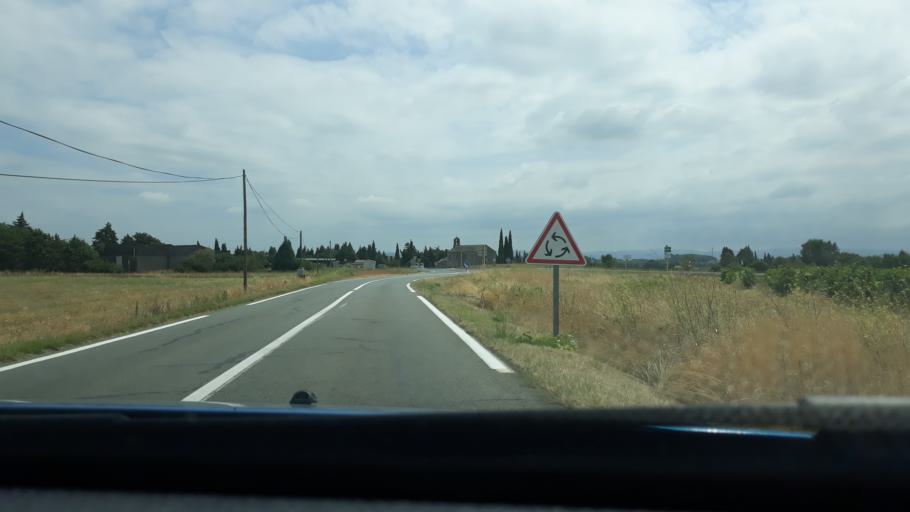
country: FR
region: Languedoc-Roussillon
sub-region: Departement de l'Aude
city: Pezens
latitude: 43.2601
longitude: 2.2482
